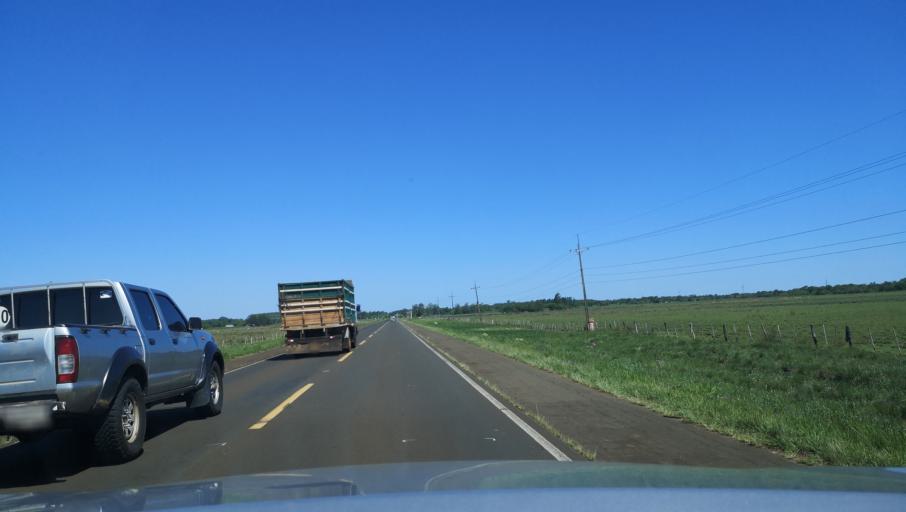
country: PY
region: Itapua
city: General Delgado
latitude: -27.0793
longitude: -56.5684
